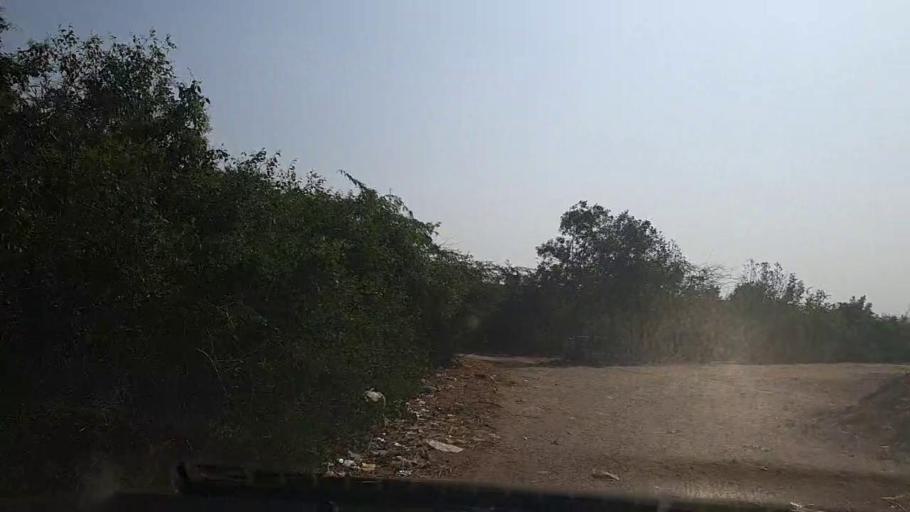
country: PK
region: Sindh
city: Thatta
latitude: 24.6494
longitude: 67.8178
